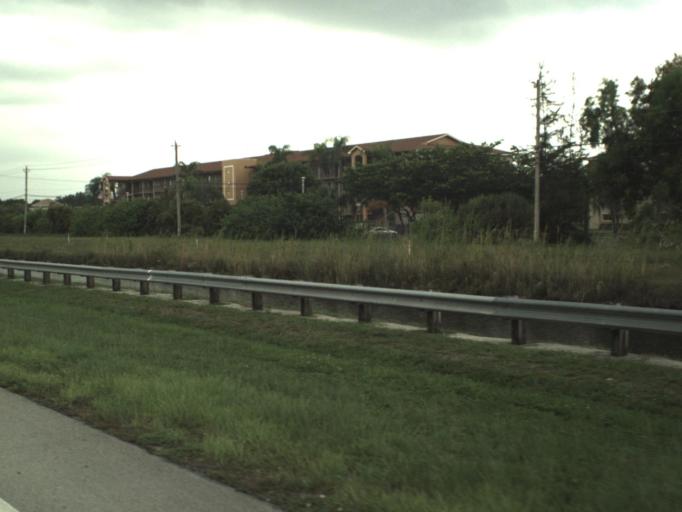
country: US
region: Florida
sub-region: Miami-Dade County
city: Country Club
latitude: 25.9955
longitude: -80.3117
